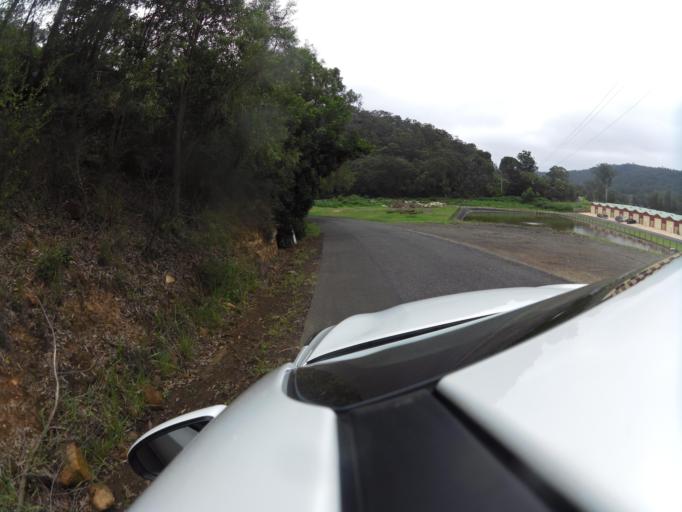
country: AU
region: New South Wales
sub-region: Hornsby Shire
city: Glenorie
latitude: -33.4030
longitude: 150.9769
